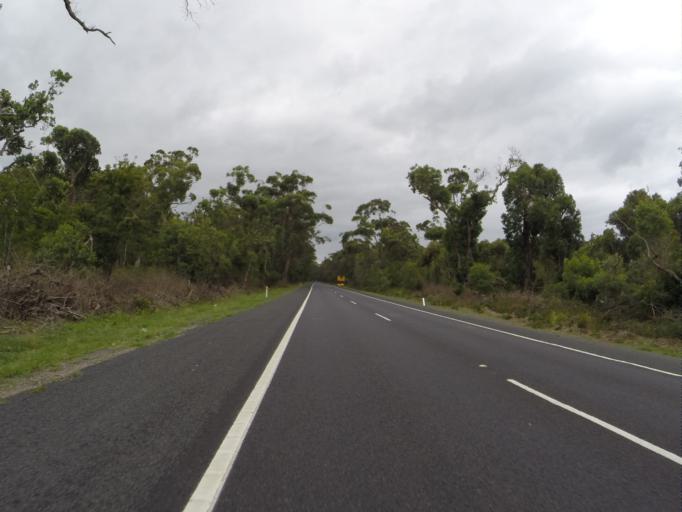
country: AU
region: New South Wales
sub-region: Shoalhaven Shire
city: Berry
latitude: -34.8257
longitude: 150.7444
